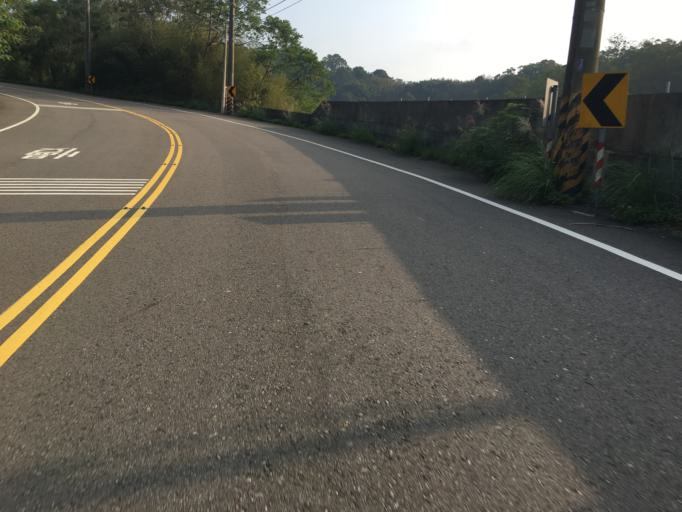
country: TW
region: Taiwan
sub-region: Hsinchu
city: Hsinchu
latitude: 24.7175
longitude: 121.0379
